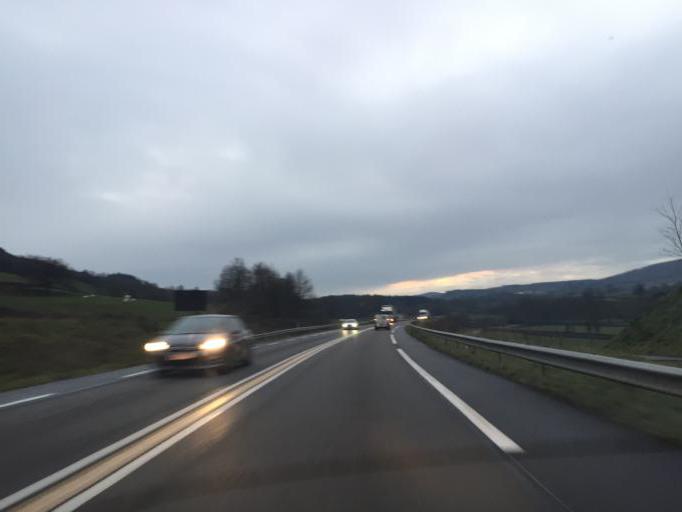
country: FR
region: Bourgogne
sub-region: Departement de Saone-et-Loire
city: Cluny
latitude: 46.3858
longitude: 4.6186
